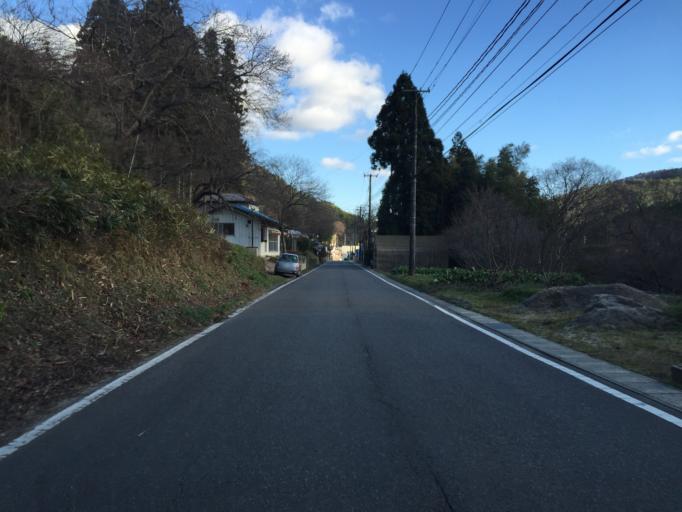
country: JP
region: Fukushima
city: Iwaki
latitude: 37.2082
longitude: 140.7469
